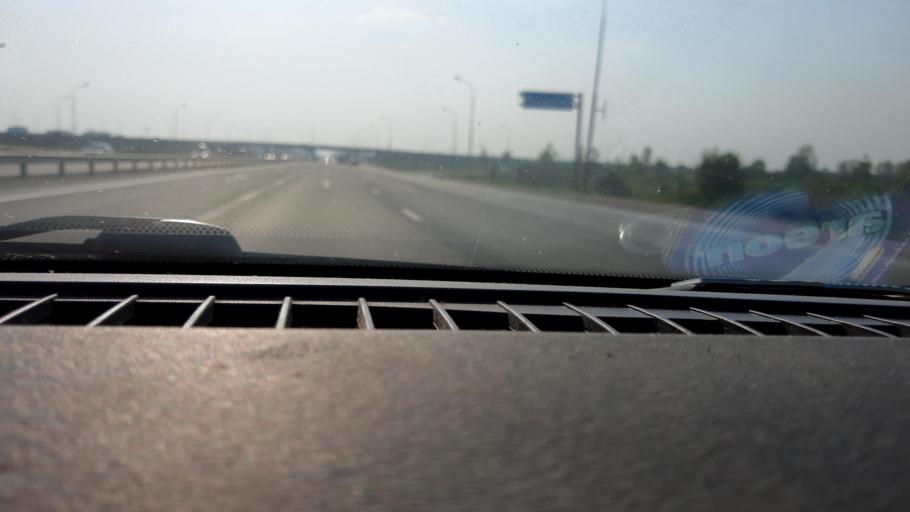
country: RU
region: Bashkortostan
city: Kabakovo
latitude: 54.6536
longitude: 56.0947
